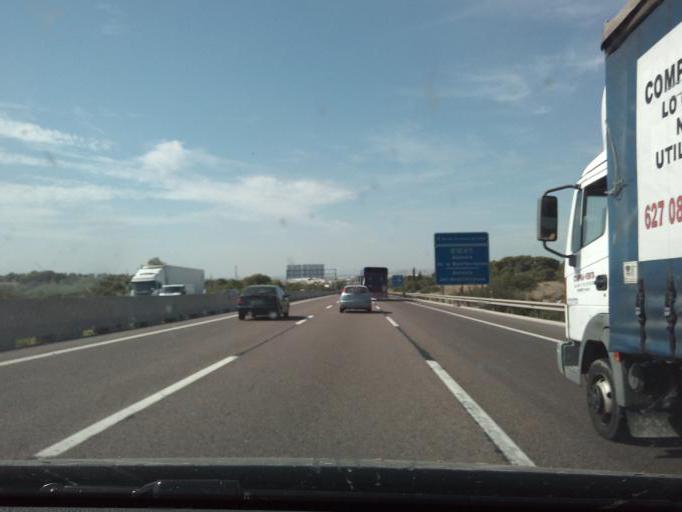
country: ES
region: Valencia
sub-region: Provincia de Valencia
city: Manises
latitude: 39.5326
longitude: -0.4613
